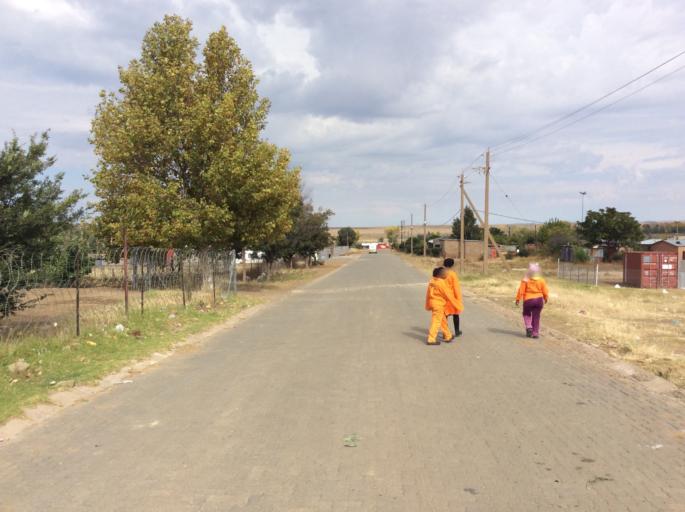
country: LS
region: Mafeteng
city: Mafeteng
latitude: -29.7201
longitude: 27.0265
